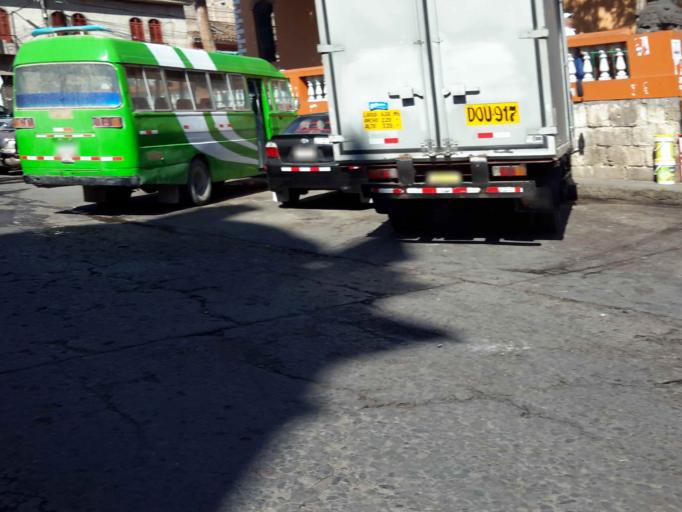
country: PE
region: Ayacucho
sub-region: Provincia de Huamanga
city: Ayacucho
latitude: -13.1634
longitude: -74.2270
